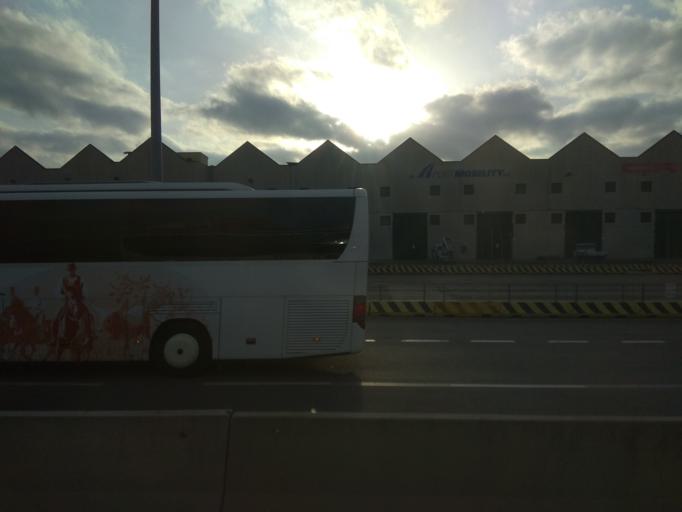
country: IT
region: Latium
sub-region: Citta metropolitana di Roma Capitale
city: Civitavecchia
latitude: 42.1020
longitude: 11.7828
